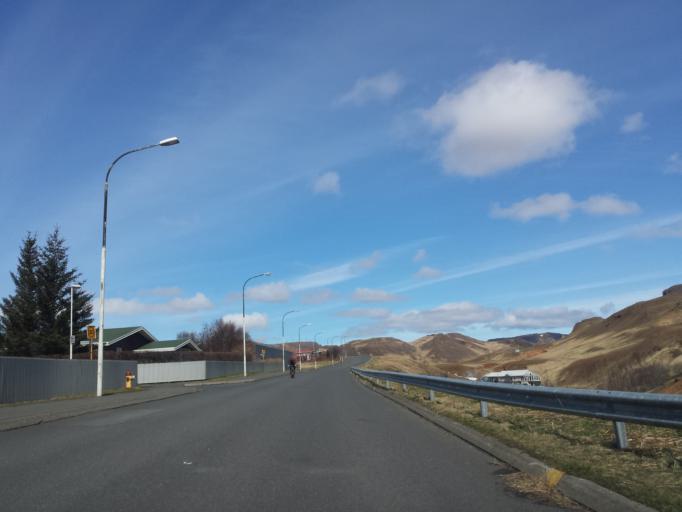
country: IS
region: South
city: Hveragerdi
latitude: 64.0030
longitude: -21.1843
